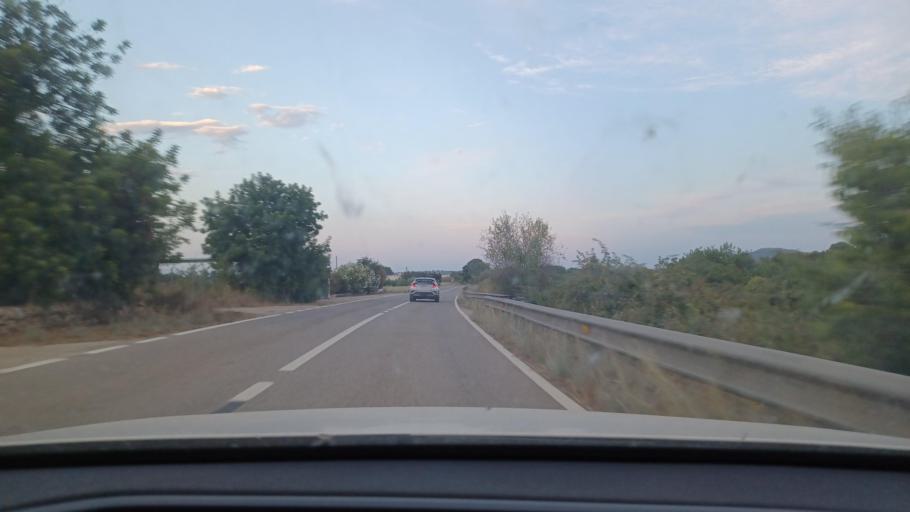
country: ES
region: Catalonia
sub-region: Provincia de Tarragona
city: Santa Barbara
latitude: 40.7157
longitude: 0.4786
